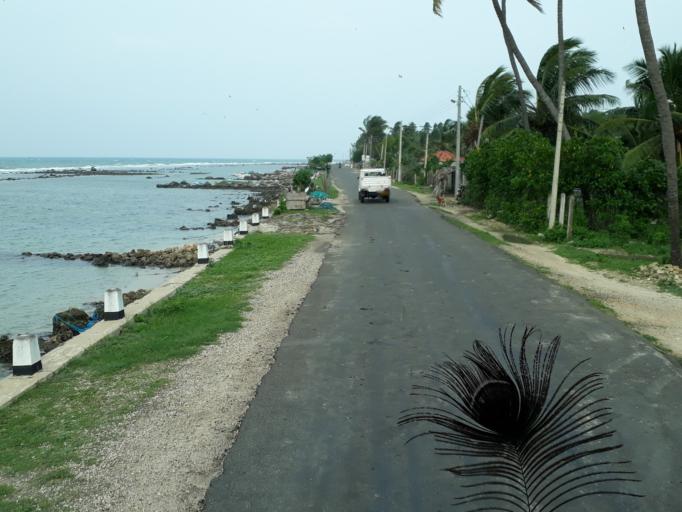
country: LK
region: Northern Province
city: Point Pedro
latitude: 9.8329
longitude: 80.2036
